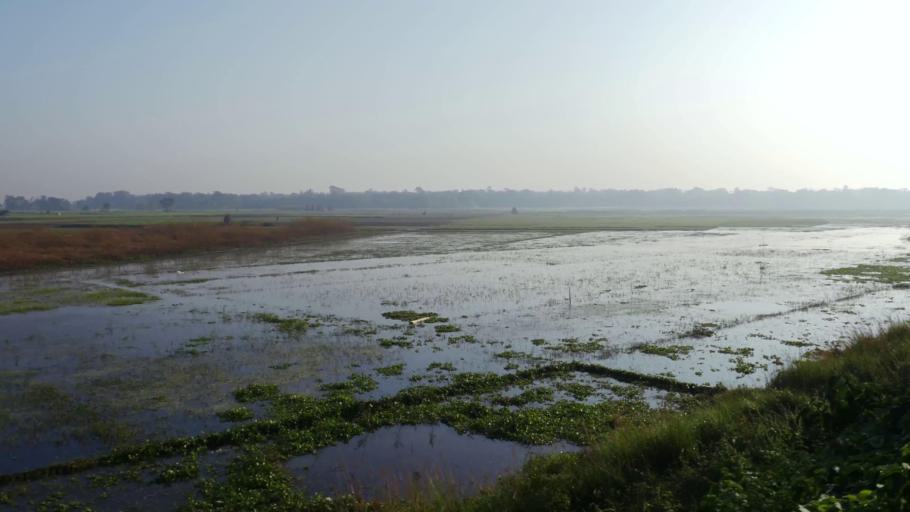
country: BD
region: Dhaka
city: Jamalpur
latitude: 24.9196
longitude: 89.9431
